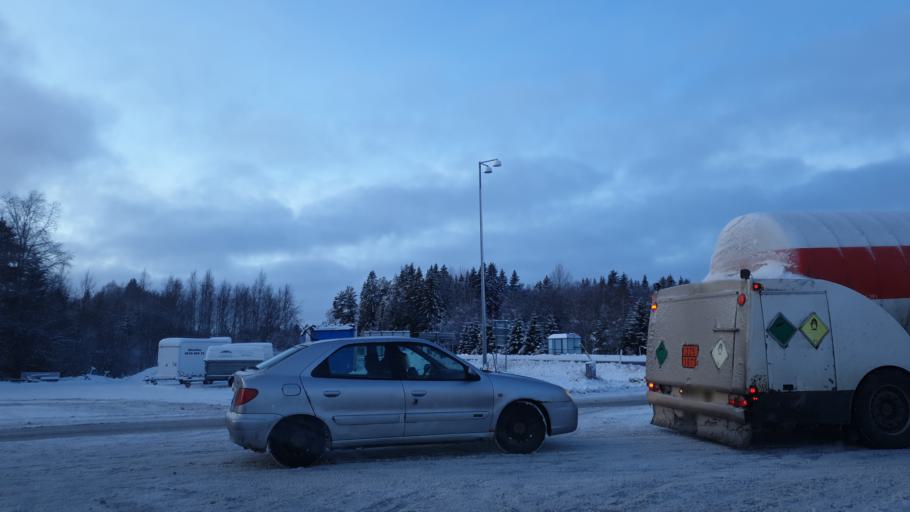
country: SE
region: Vaesterbotten
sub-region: Umea Kommun
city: Hoernefors
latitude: 63.6382
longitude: 19.9111
